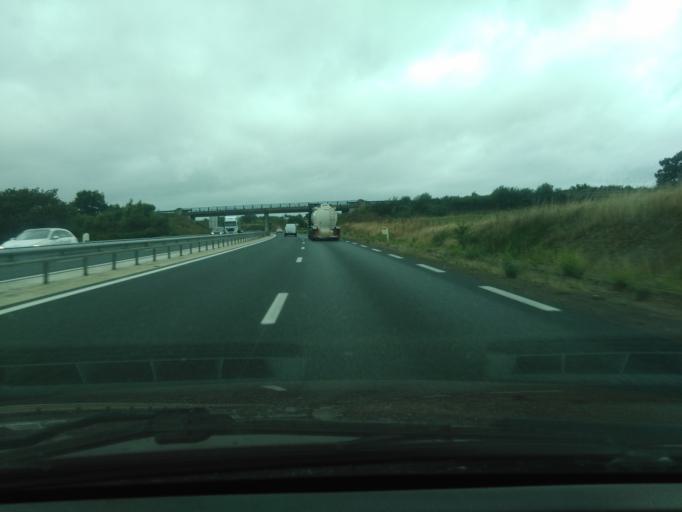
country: FR
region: Pays de la Loire
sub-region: Departement de la Vendee
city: Dompierre-sur-Yon
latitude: 46.6776
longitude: -1.3683
